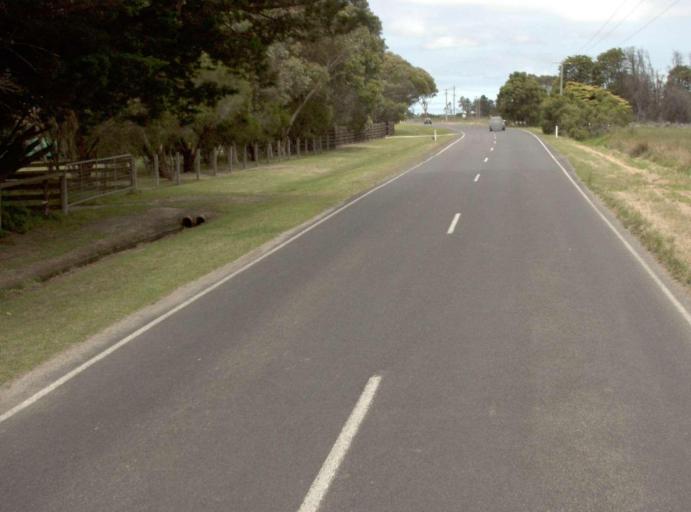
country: AU
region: Victoria
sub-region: Latrobe
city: Traralgon
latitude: -38.5505
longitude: 146.6546
